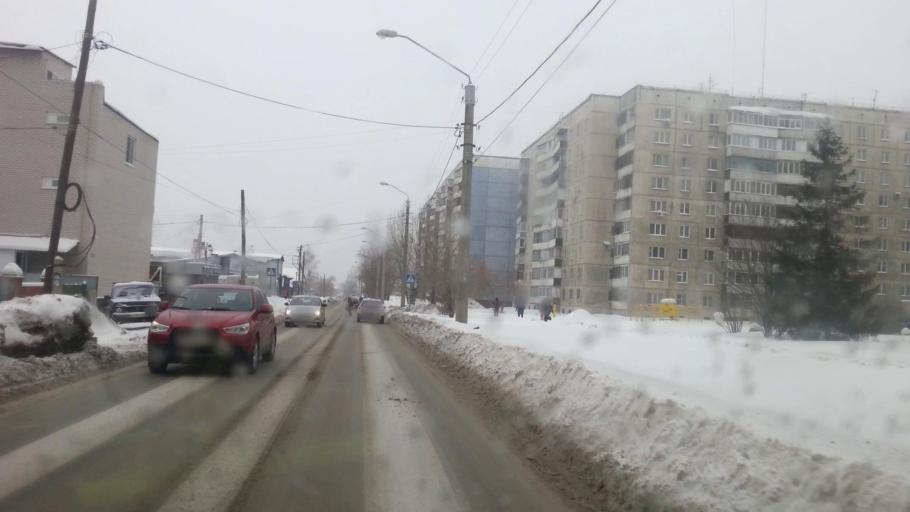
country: RU
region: Altai Krai
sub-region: Gorod Barnaulskiy
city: Barnaul
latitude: 53.3343
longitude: 83.7711
